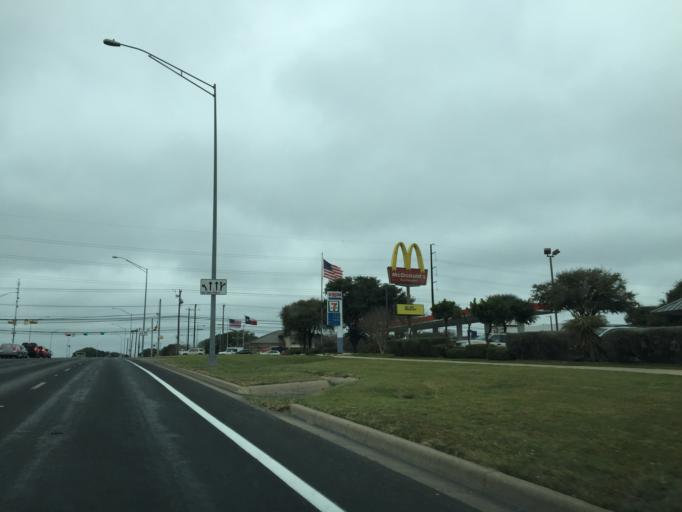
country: US
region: Texas
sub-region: Travis County
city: Wells Branch
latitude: 30.3909
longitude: -97.7204
